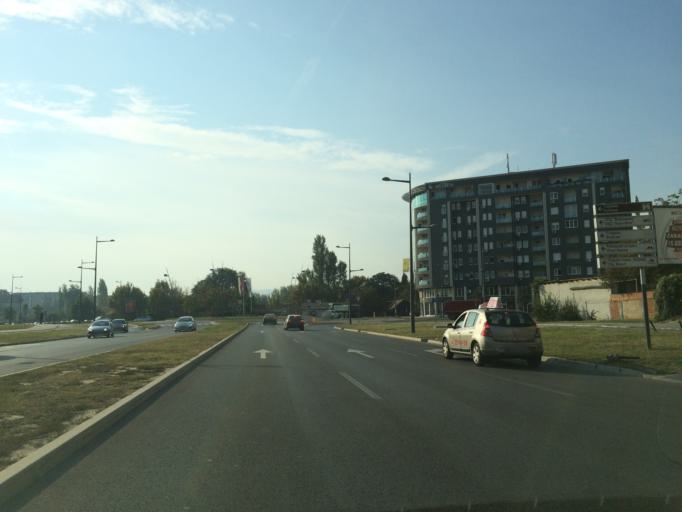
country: RS
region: Autonomna Pokrajina Vojvodina
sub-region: Juznobacki Okrug
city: Novi Sad
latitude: 45.2406
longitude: 19.8220
